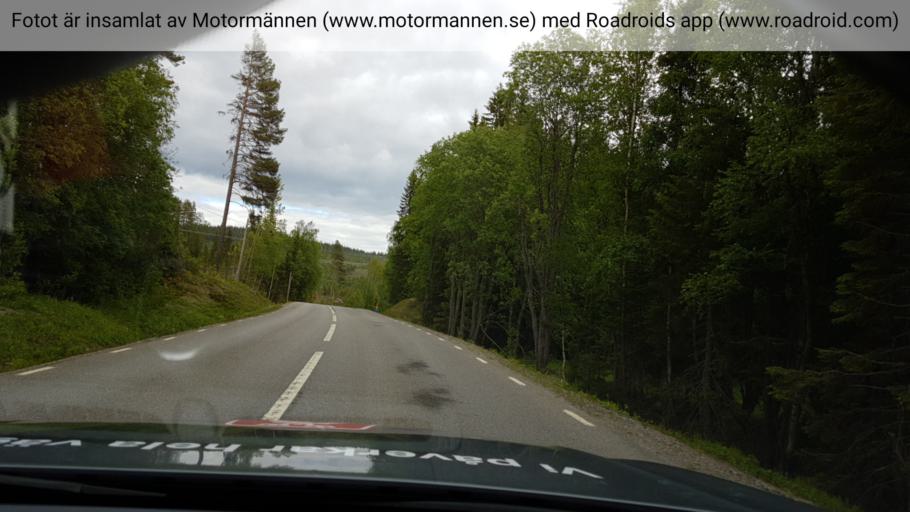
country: SE
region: Jaemtland
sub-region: Stroemsunds Kommun
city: Stroemsund
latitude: 64.3454
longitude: 14.8090
